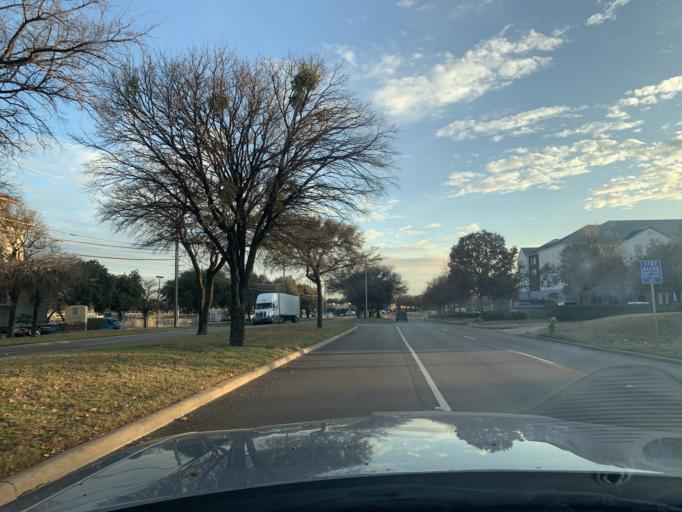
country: US
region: Texas
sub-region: Tarrant County
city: Euless
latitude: 32.8355
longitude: -97.0221
